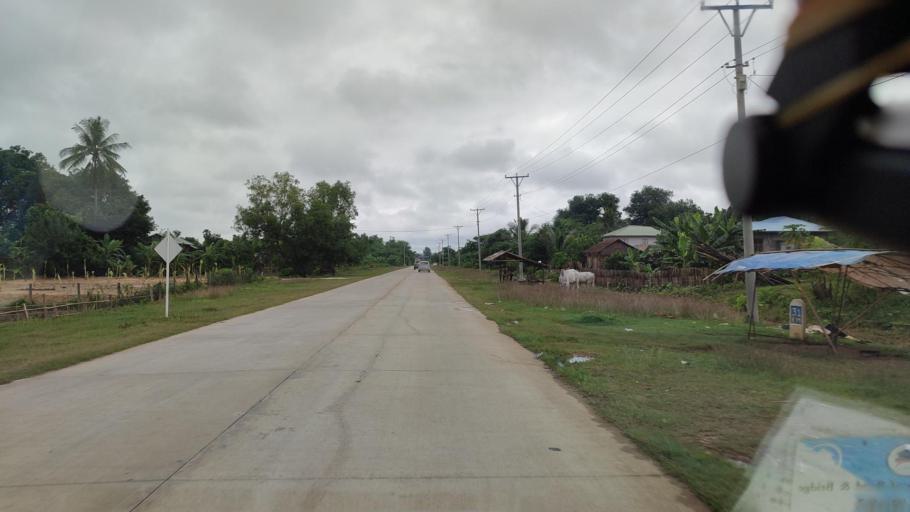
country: MM
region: Mandalay
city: Nay Pyi Taw
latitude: 19.8749
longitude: 96.0231
